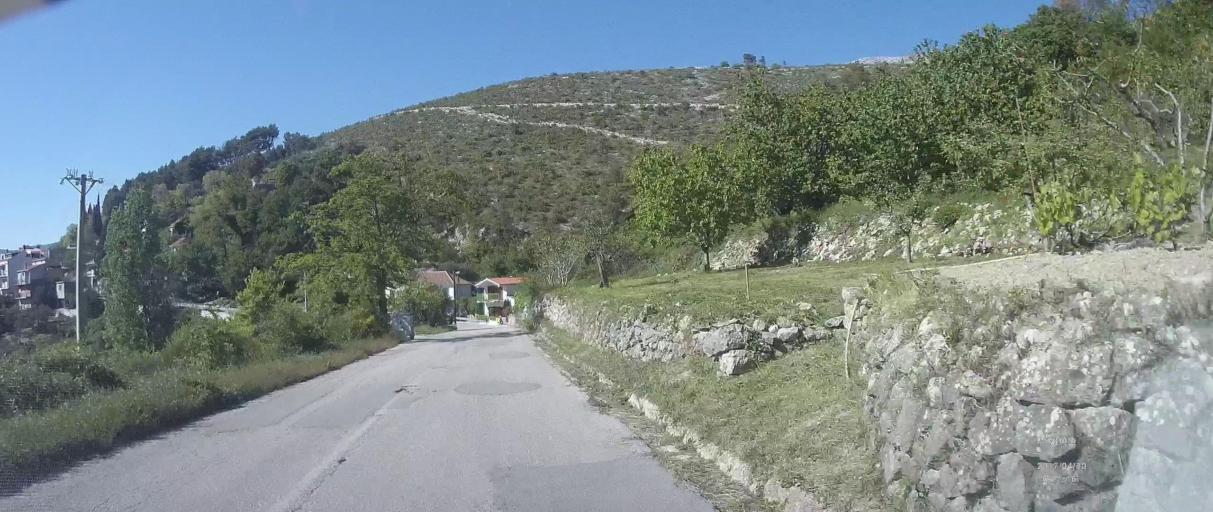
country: HR
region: Splitsko-Dalmatinska
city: Srinjine
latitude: 43.5047
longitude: 16.5990
